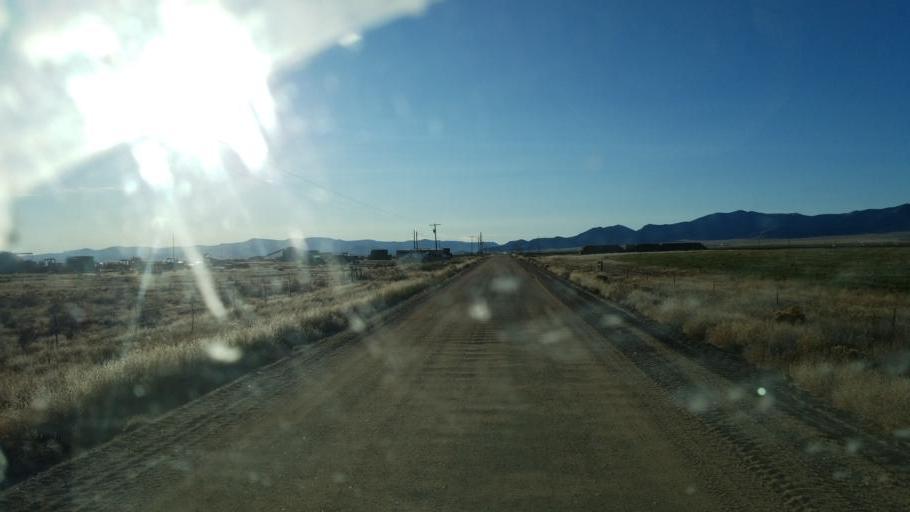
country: US
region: Colorado
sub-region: Saguache County
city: Saguache
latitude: 38.1005
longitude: -105.9143
